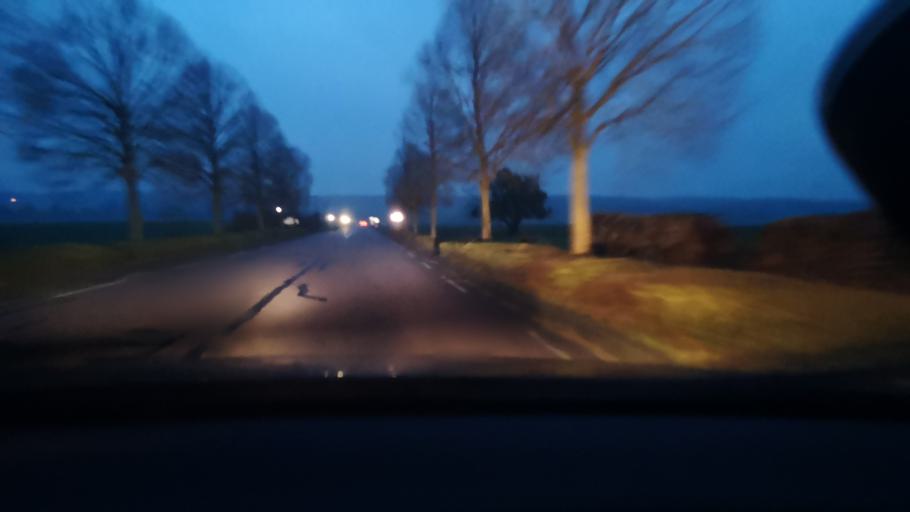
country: FR
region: Bourgogne
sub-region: Departement de Saone-et-Loire
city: Demigny
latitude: 46.9212
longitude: 4.8373
